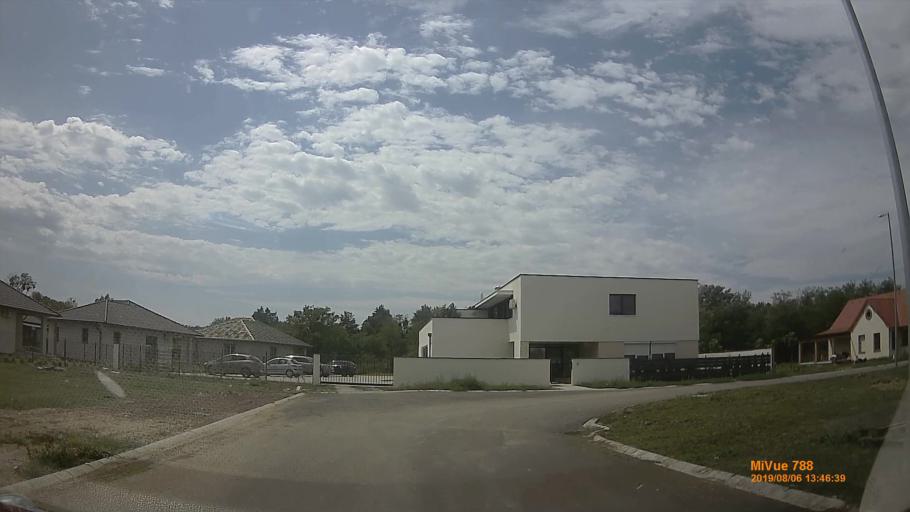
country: HU
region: Vas
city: Szombathely
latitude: 47.2509
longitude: 16.5994
